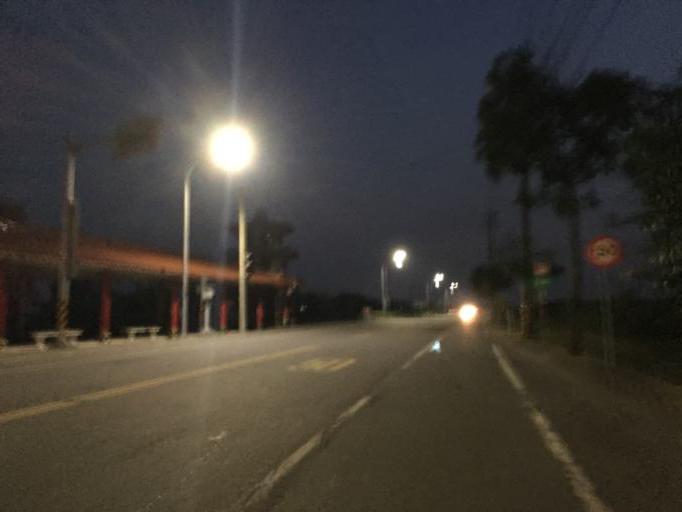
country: TW
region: Taiwan
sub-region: Chiayi
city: Taibao
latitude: 23.5243
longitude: 120.3221
